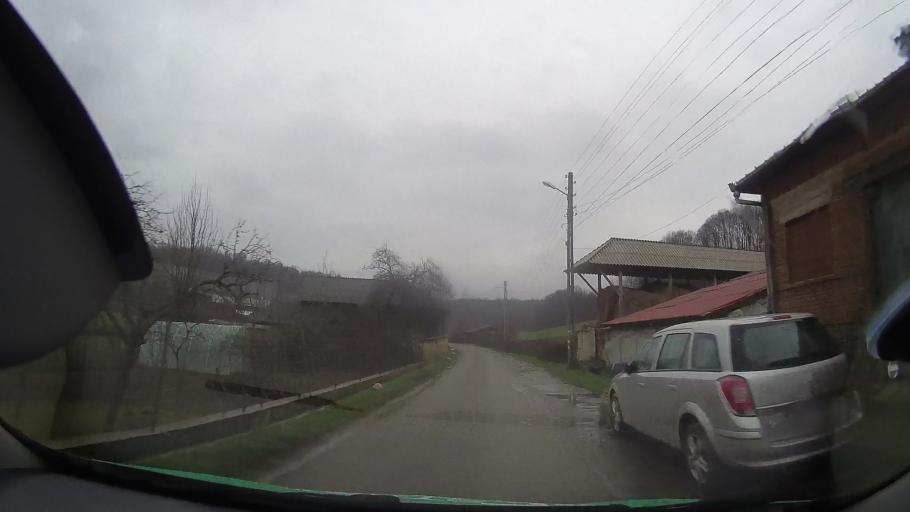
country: RO
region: Bihor
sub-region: Comuna Uileacu de Beius
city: Forau
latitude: 46.7159
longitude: 22.2292
